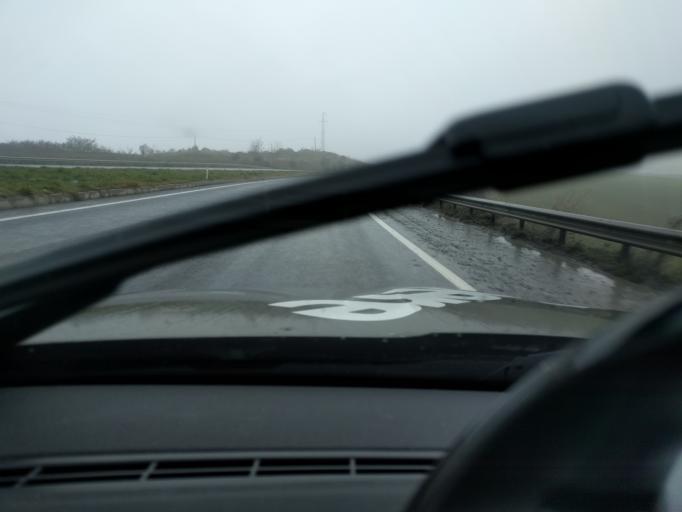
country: TR
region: Istanbul
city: Boyalik
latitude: 41.2803
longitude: 28.6331
